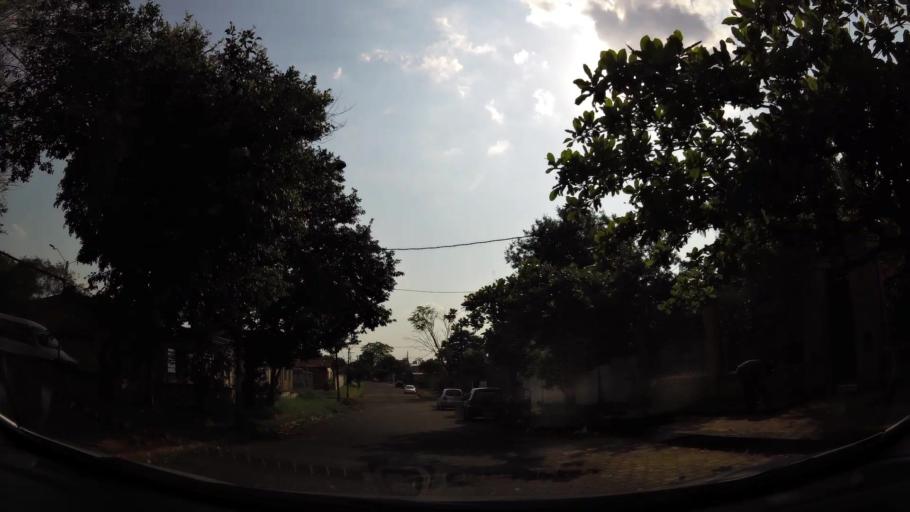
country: PY
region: Alto Parana
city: Presidente Franco
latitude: -25.5256
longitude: -54.6218
